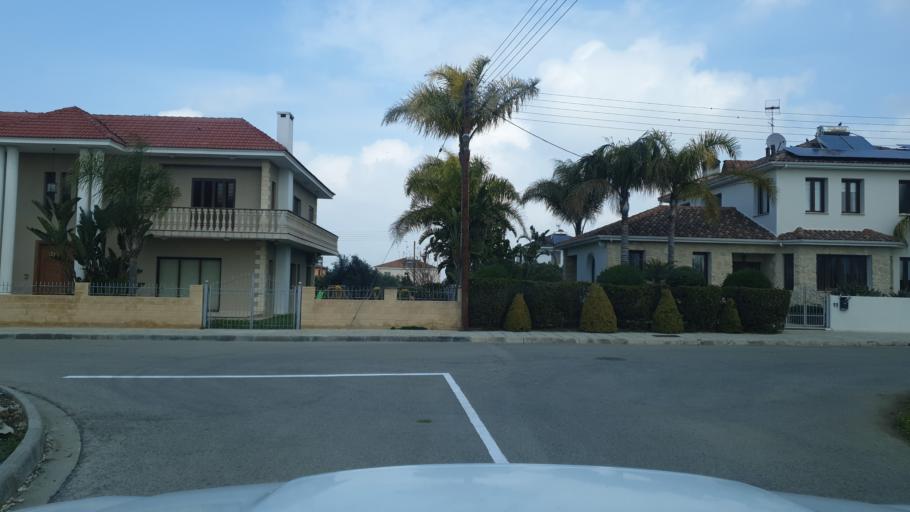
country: CY
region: Lefkosia
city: Kato Deftera
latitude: 35.0864
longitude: 33.2890
